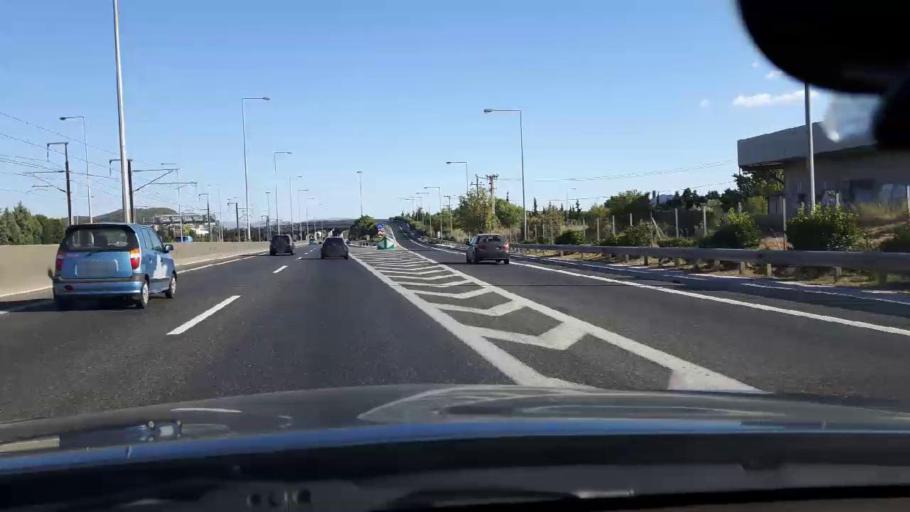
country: GR
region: Attica
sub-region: Nomarchia Anatolikis Attikis
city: Pallini
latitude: 37.9871
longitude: 23.8706
